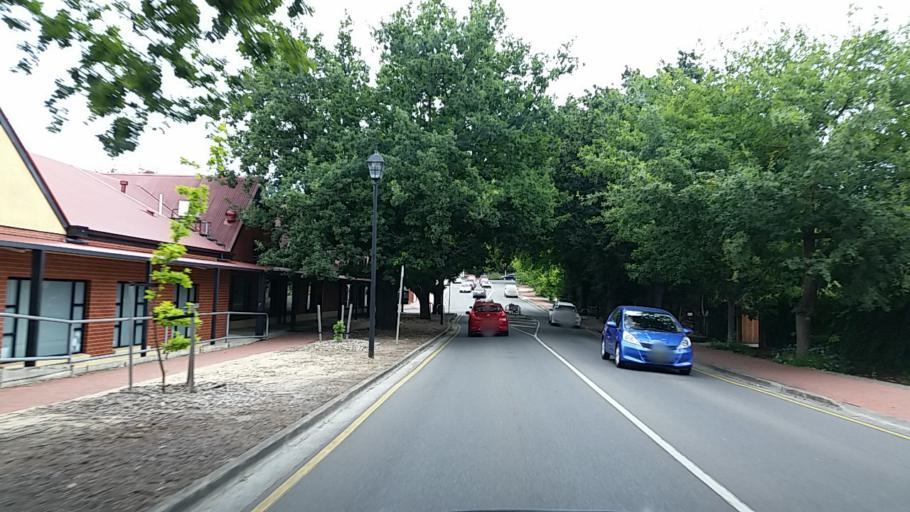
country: AU
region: South Australia
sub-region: Mount Barker
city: Mount Barker
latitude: -35.0646
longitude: 138.8571
